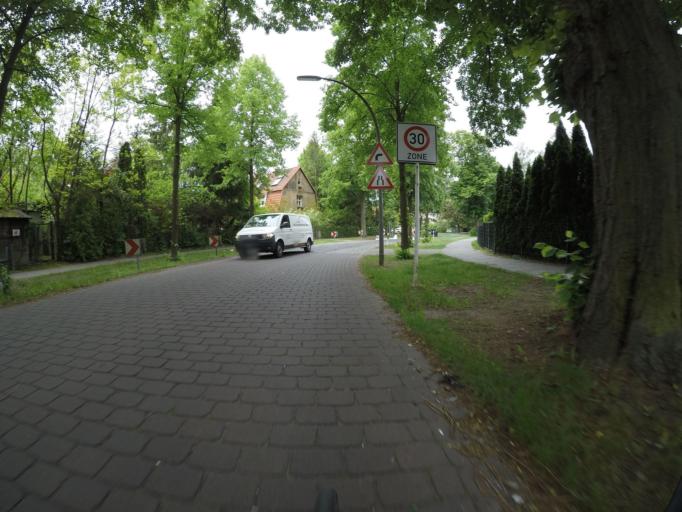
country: DE
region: Brandenburg
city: Glienicke
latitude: 52.6258
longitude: 13.3272
